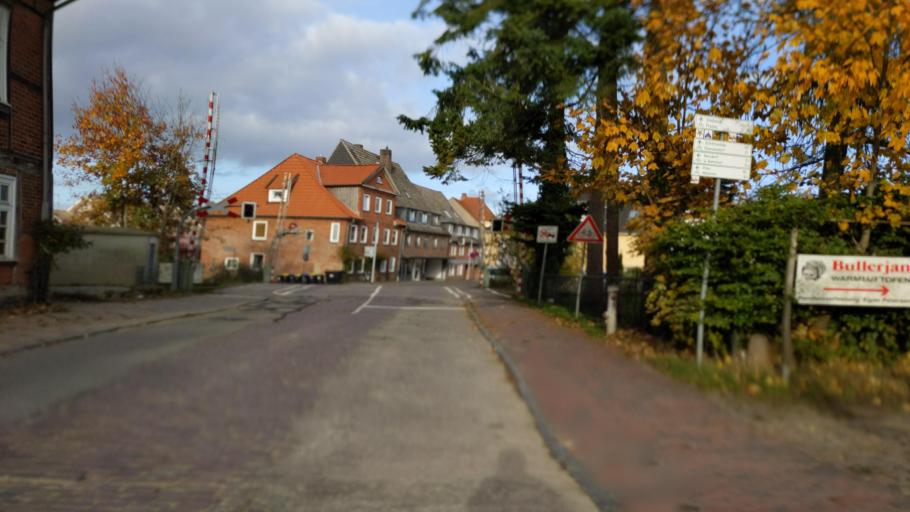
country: DE
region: Schleswig-Holstein
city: Eutin
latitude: 54.1320
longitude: 10.6175
